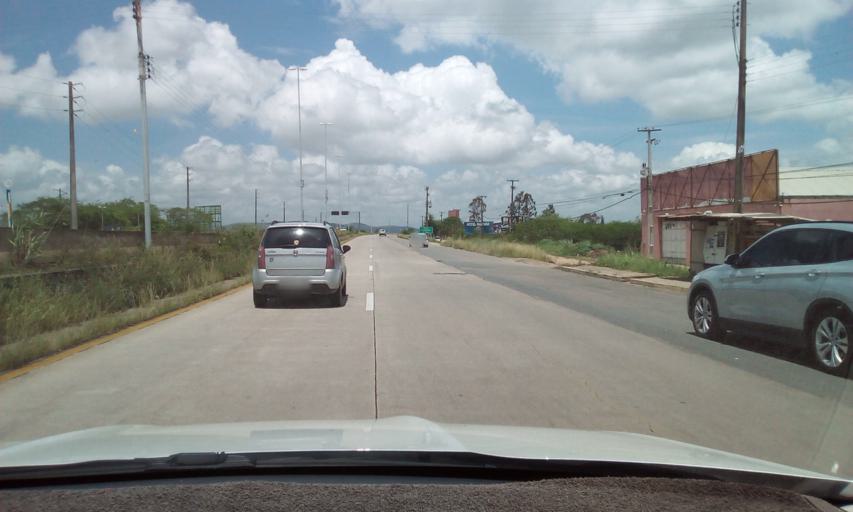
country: BR
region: Pernambuco
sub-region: Gravata
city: Gravata
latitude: -8.2016
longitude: -35.5931
